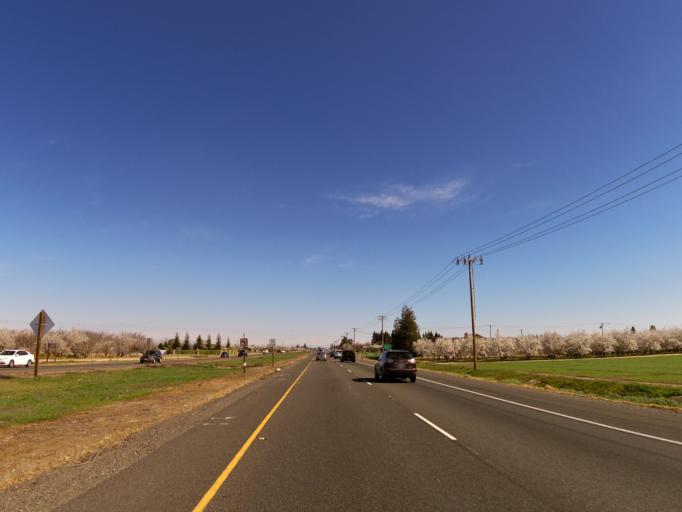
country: US
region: California
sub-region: Stanislaus County
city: Salida
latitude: 37.7111
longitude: -121.0661
